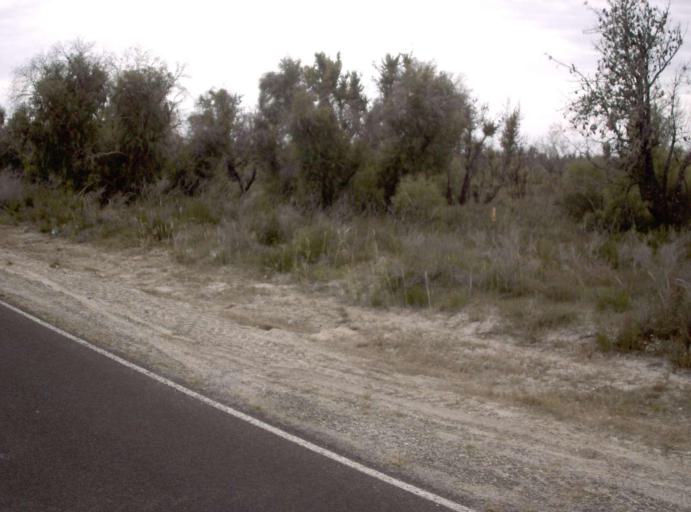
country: AU
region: Victoria
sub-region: East Gippsland
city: Bairnsdale
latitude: -38.1051
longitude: 147.4845
